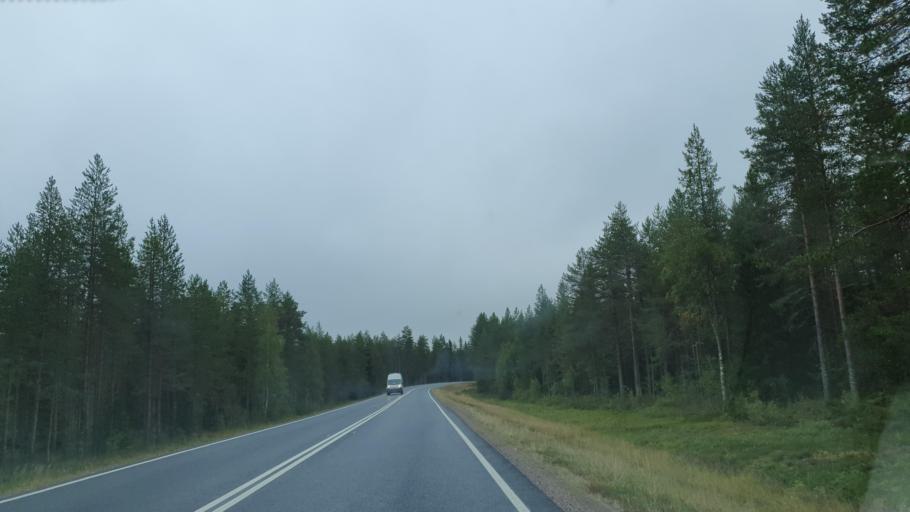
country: FI
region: Northern Ostrobothnia
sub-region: Oulunkaari
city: Pudasjaervi
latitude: 65.3508
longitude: 27.3933
